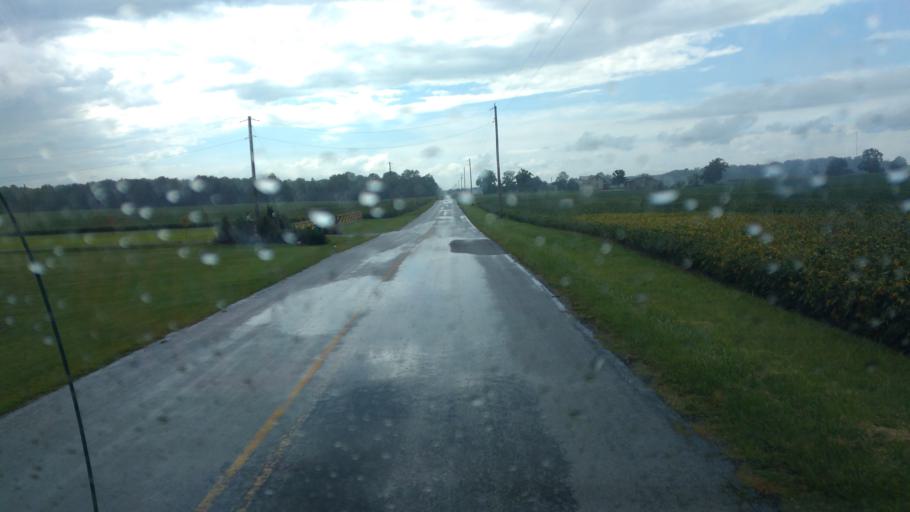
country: US
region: Ohio
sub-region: Hardin County
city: Kenton
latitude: 40.7034
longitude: -83.6075
